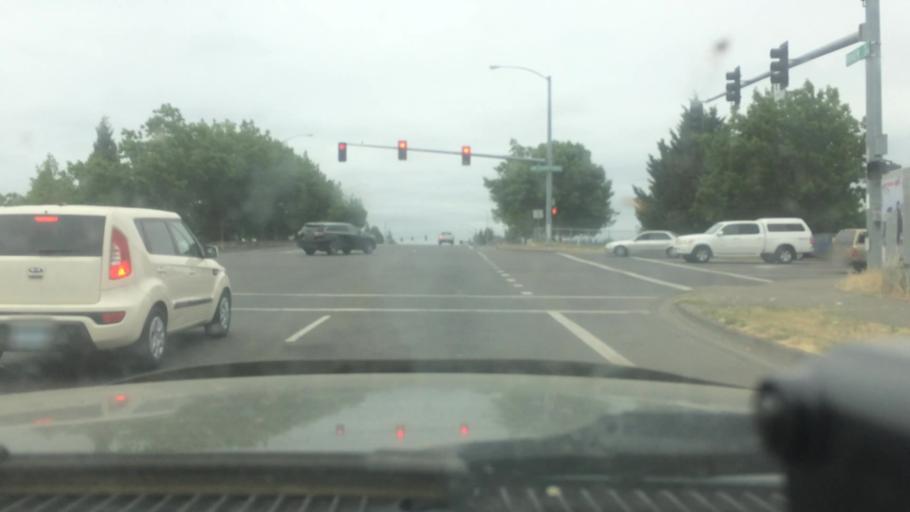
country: US
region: Oregon
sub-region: Lane County
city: Eugene
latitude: 44.0643
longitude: -123.1174
